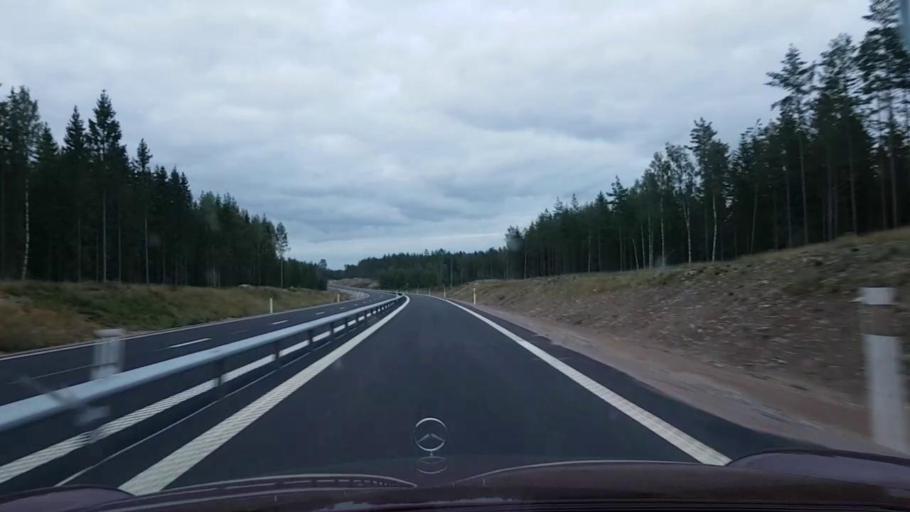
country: SE
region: Vaestmanland
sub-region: Surahammars Kommun
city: Surahammar
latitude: 59.6720
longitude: 16.2291
